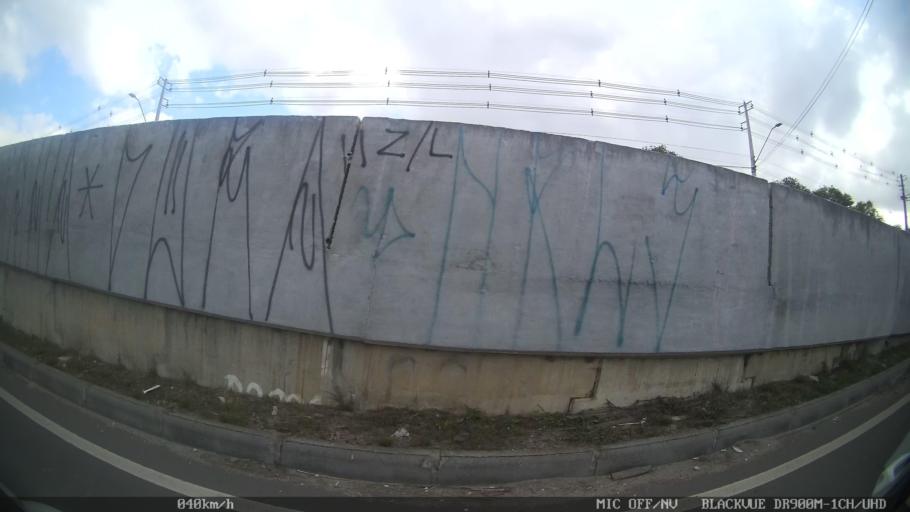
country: BR
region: Parana
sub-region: Pinhais
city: Pinhais
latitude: -25.4360
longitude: -49.1623
